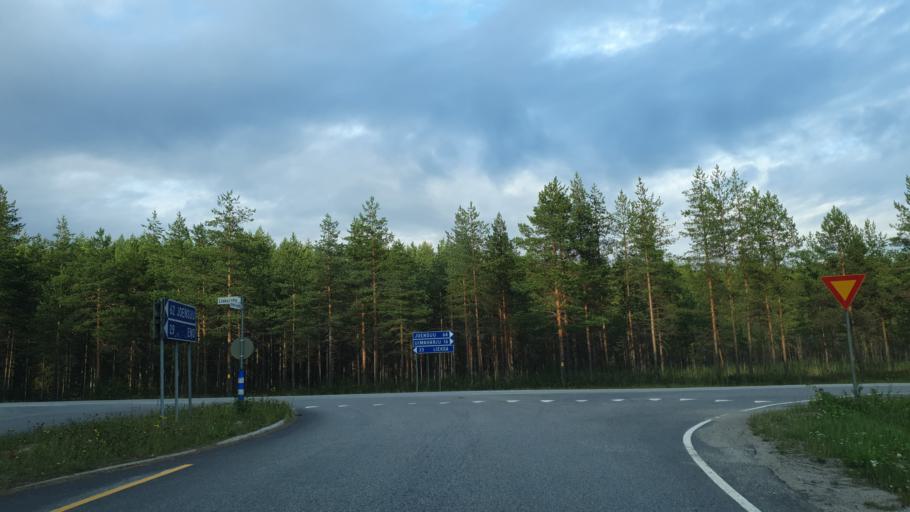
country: FI
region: North Karelia
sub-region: Joensuu
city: Eno
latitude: 63.0438
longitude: 30.1253
